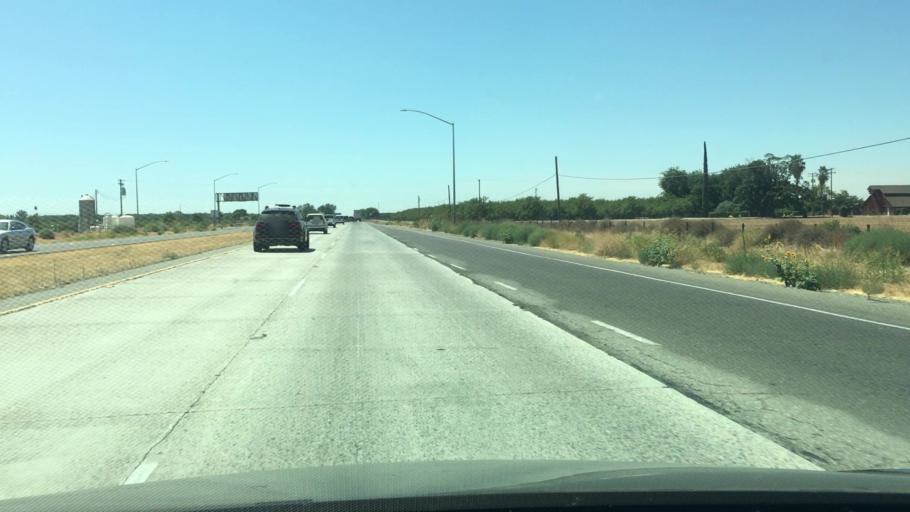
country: US
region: California
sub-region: Madera County
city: Chowchilla
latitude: 37.0836
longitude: -120.2994
